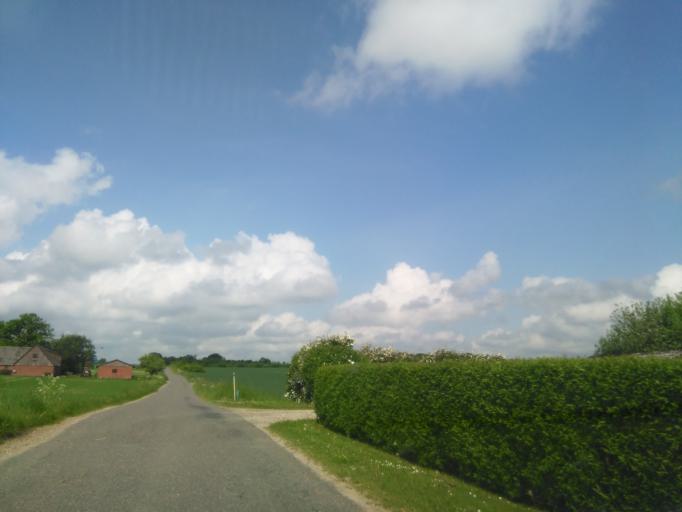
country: DK
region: Central Jutland
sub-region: Skanderborg Kommune
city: Skovby
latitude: 56.2046
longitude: 9.9535
